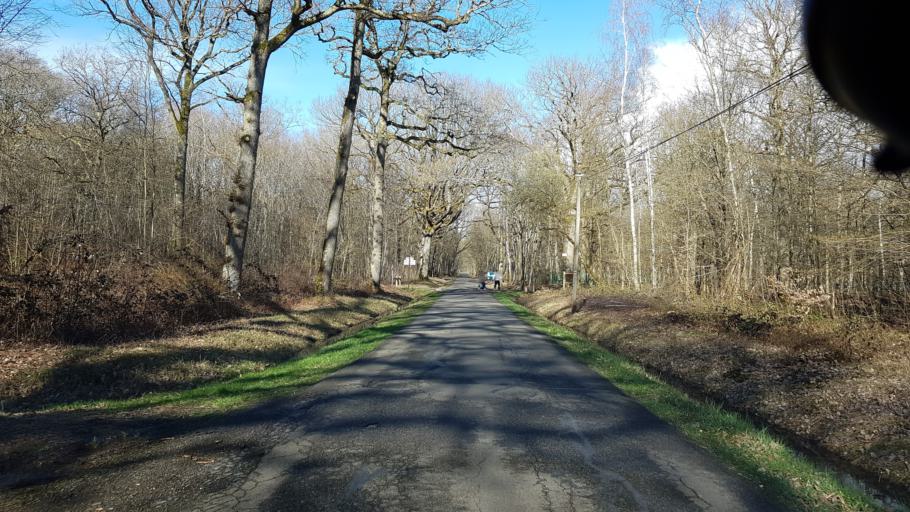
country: FR
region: Ile-de-France
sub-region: Departement des Yvelines
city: Rambouillet
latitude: 48.6187
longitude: 1.8607
